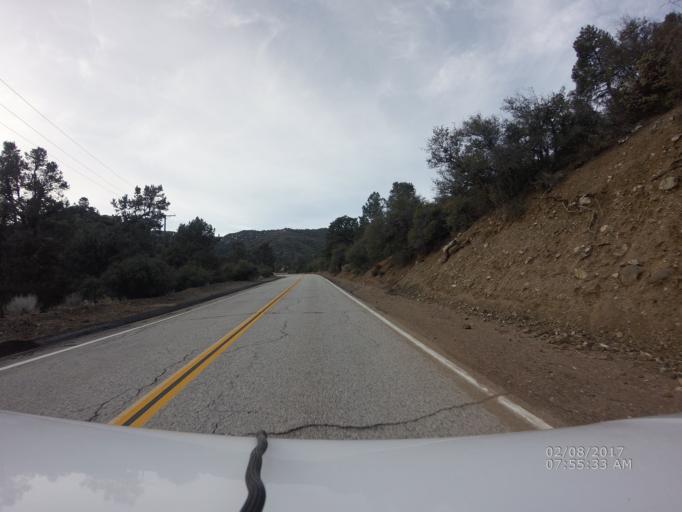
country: US
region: California
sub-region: San Bernardino County
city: Pinon Hills
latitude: 34.4158
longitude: -117.7689
